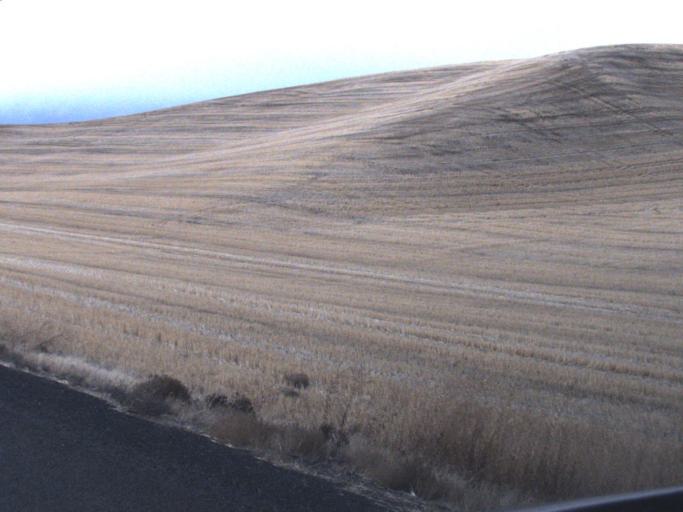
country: US
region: Washington
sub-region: Whitman County
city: Colfax
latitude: 46.8592
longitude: -117.4561
